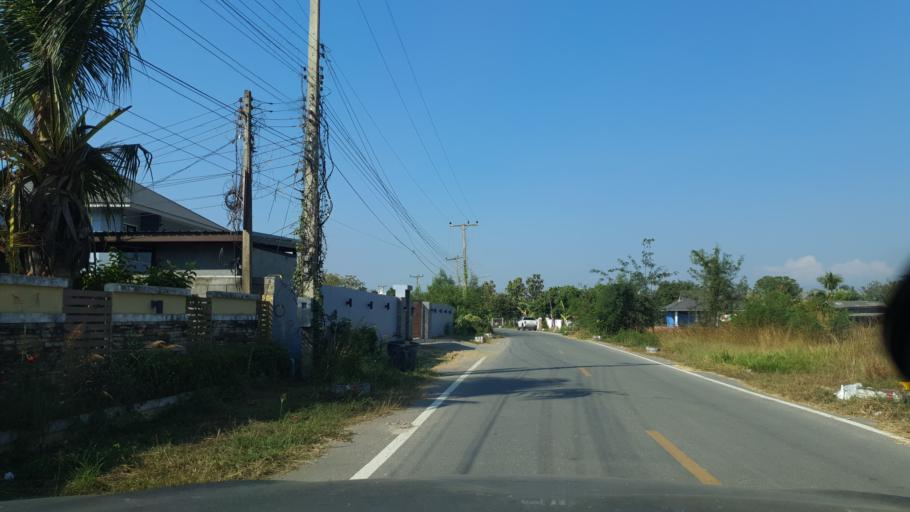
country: TH
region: Lamphun
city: Ban Thi
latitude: 18.6851
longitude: 99.1139
